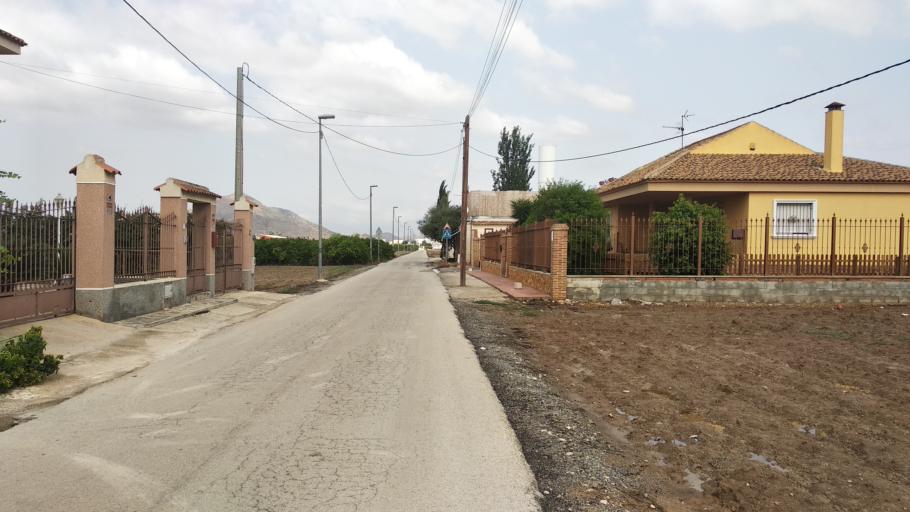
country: ES
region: Murcia
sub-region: Murcia
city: Santomera
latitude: 38.0375
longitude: -1.0384
